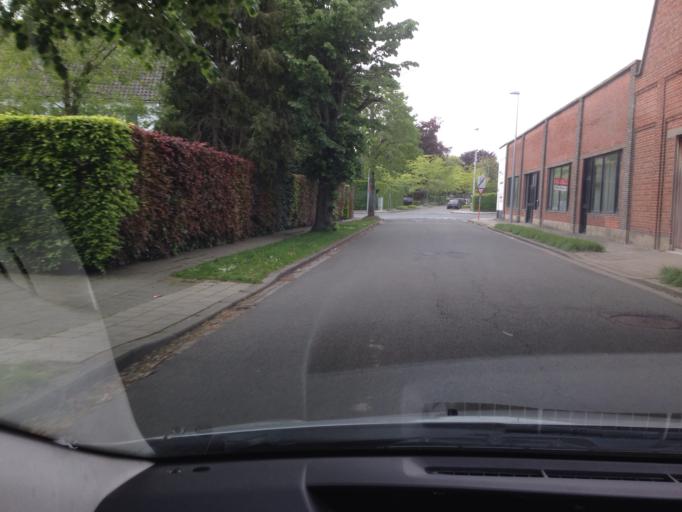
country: BE
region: Flanders
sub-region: Provincie West-Vlaanderen
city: Roeselare
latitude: 50.9567
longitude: 3.1237
